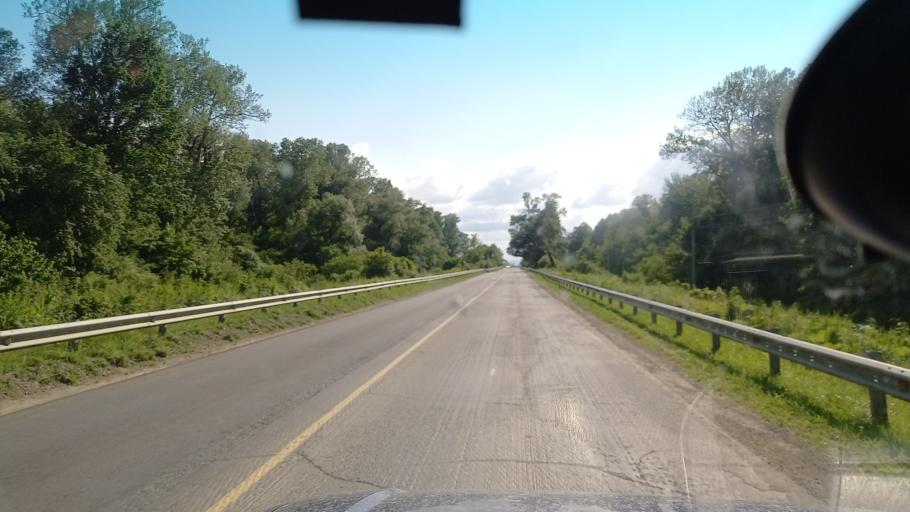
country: RU
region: Krasnodarskiy
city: Mostovskoy
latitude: 44.4031
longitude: 40.8292
